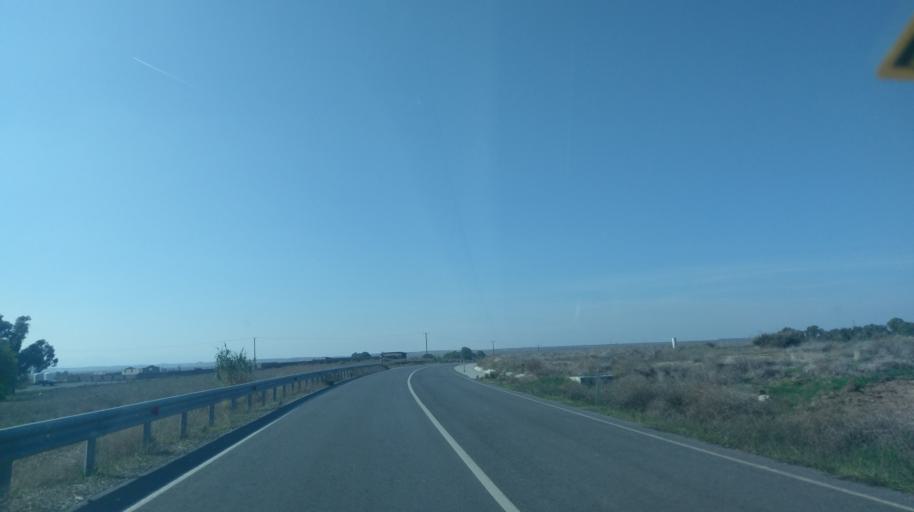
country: CY
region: Larnaka
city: Athienou
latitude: 35.1221
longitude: 33.5160
